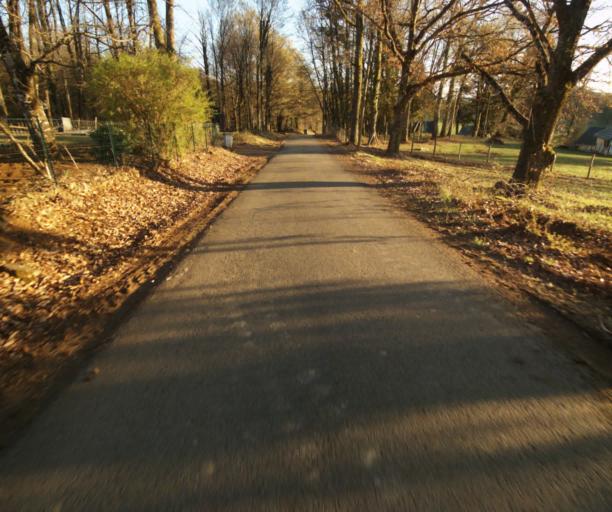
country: FR
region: Limousin
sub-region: Departement de la Correze
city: Seilhac
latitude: 45.3479
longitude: 1.7142
